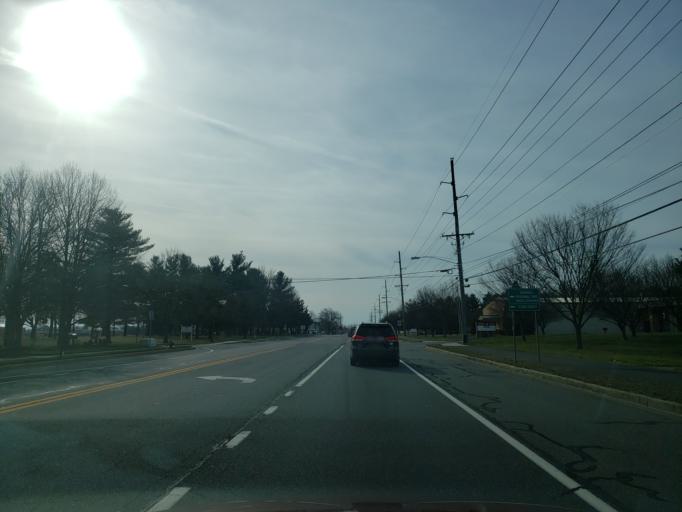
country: US
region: Delaware
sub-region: Kent County
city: Dover
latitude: 39.1643
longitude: -75.5448
